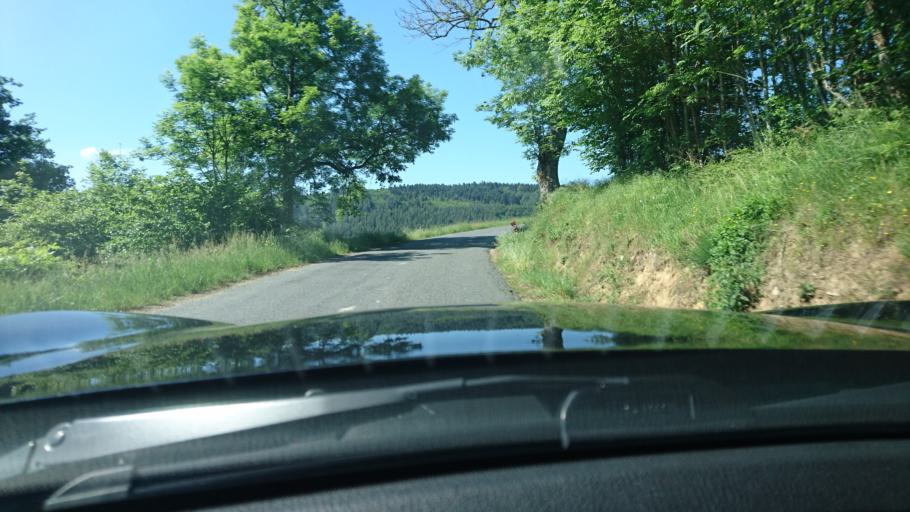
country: FR
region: Rhone-Alpes
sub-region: Departement de la Loire
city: Violay
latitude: 45.8285
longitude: 4.3819
